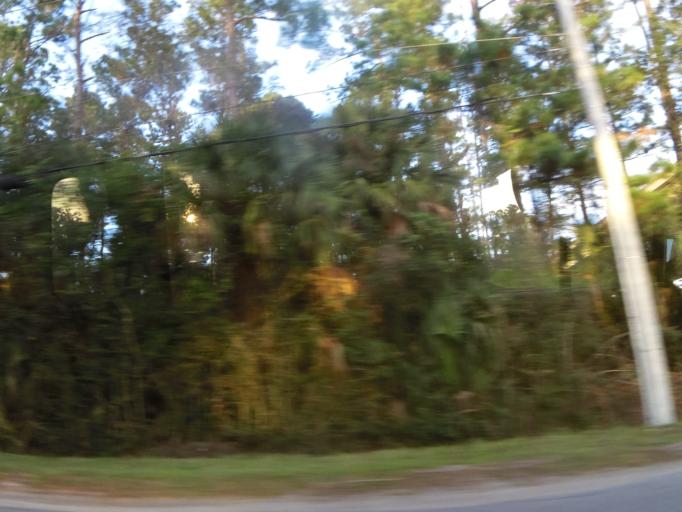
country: US
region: Florida
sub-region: Saint Johns County
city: Palm Valley
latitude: 30.1341
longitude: -81.3845
